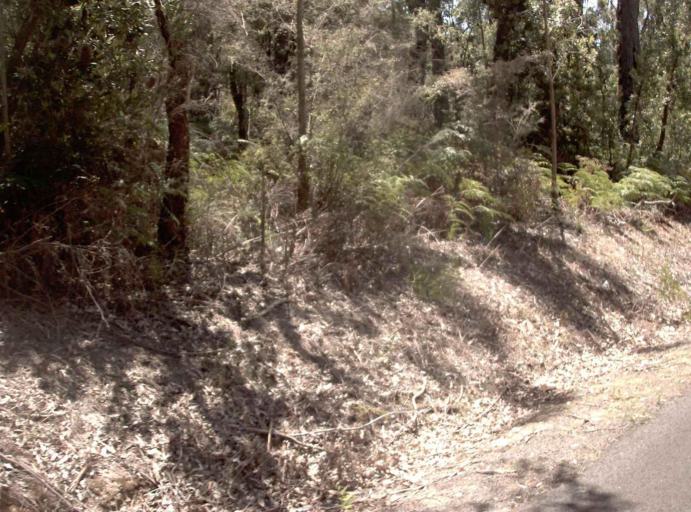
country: AU
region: Victoria
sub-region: East Gippsland
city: Lakes Entrance
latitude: -37.7434
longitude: 148.0755
